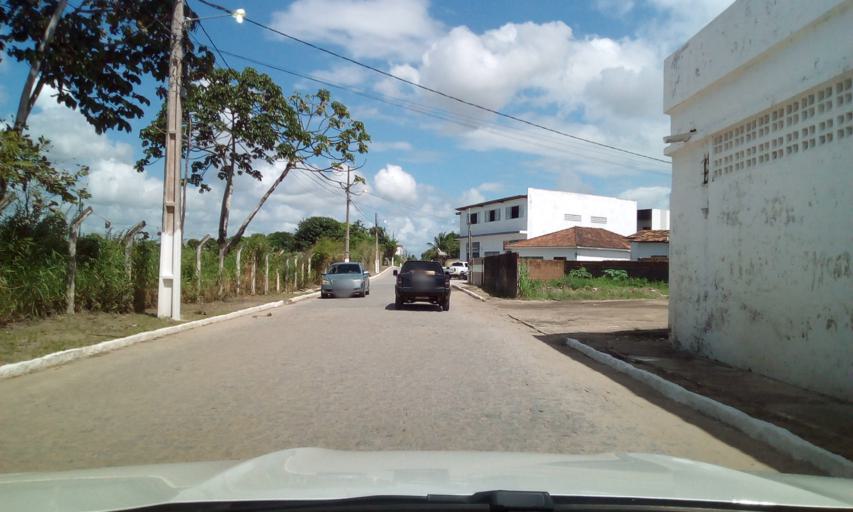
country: BR
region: Paraiba
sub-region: Santa Rita
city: Santa Rita
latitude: -7.1373
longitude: -34.9645
